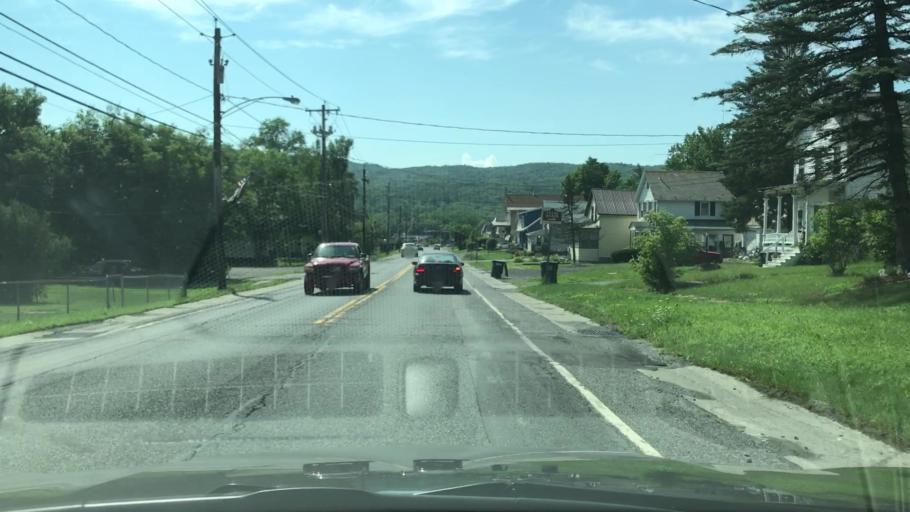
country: US
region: New York
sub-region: Washington County
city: Whitehall
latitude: 43.5501
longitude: -73.3928
